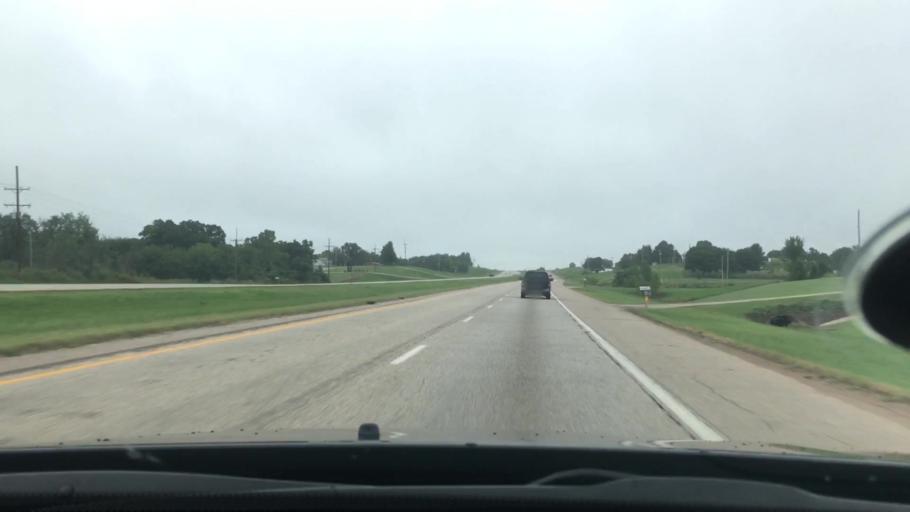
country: US
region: Oklahoma
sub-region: Seminole County
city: Seminole
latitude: 35.2986
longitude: -96.6708
